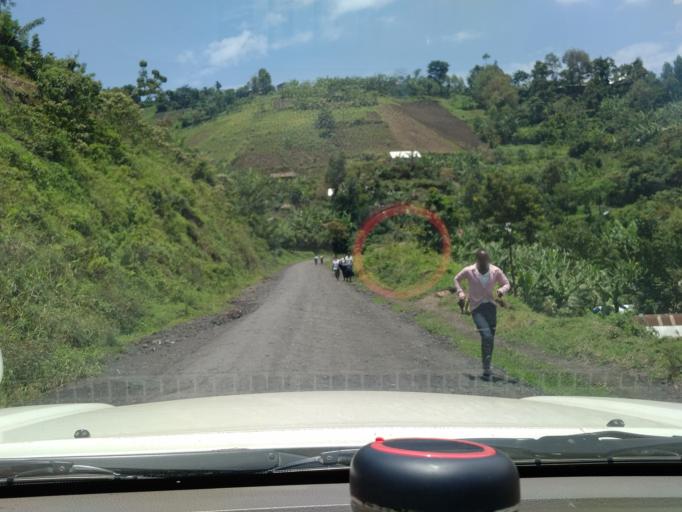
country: CD
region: Nord Kivu
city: Sake
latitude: -1.7519
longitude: 28.9874
